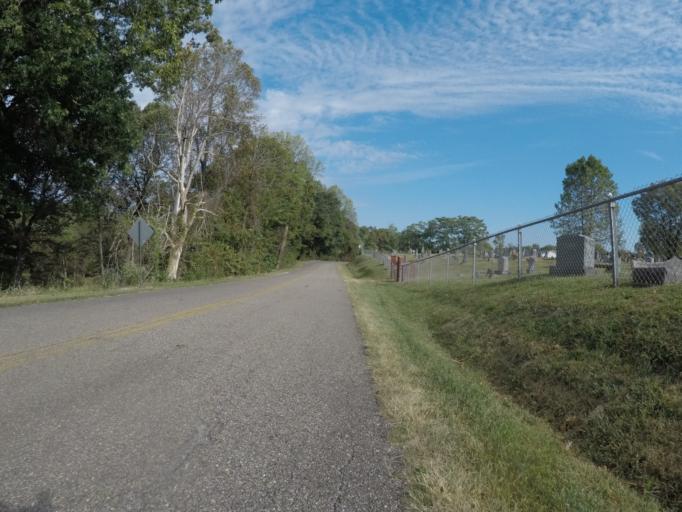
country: US
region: West Virginia
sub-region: Cabell County
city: Lesage
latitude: 38.5674
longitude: -82.4269
